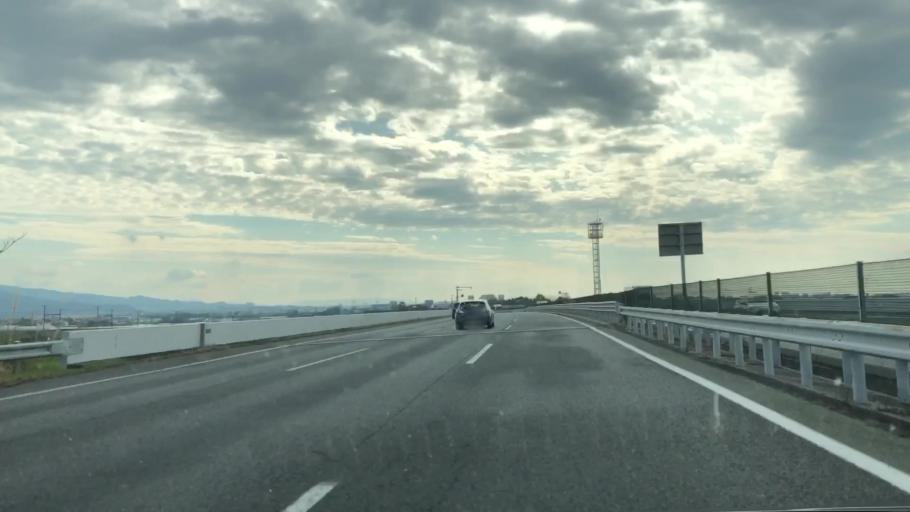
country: JP
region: Saga Prefecture
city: Tosu
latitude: 33.3545
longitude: 130.5382
